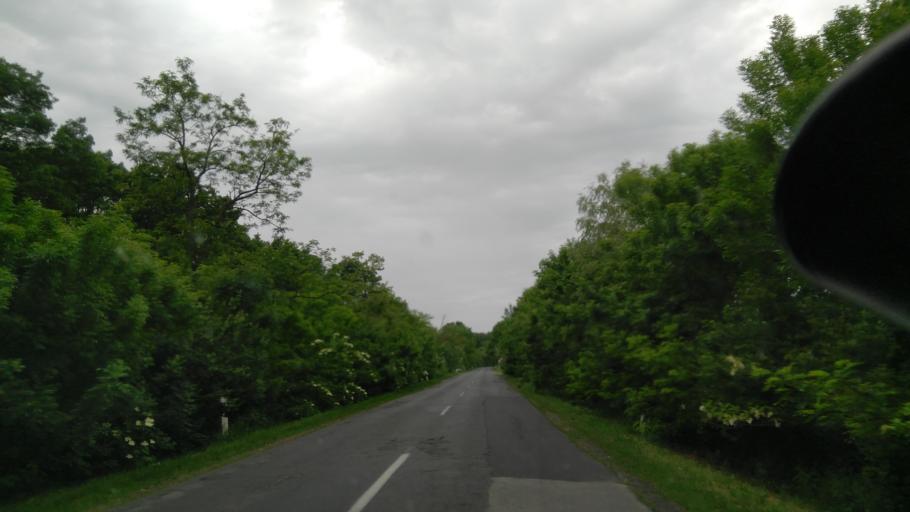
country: HU
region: Bekes
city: Doboz
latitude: 46.7232
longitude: 21.3018
